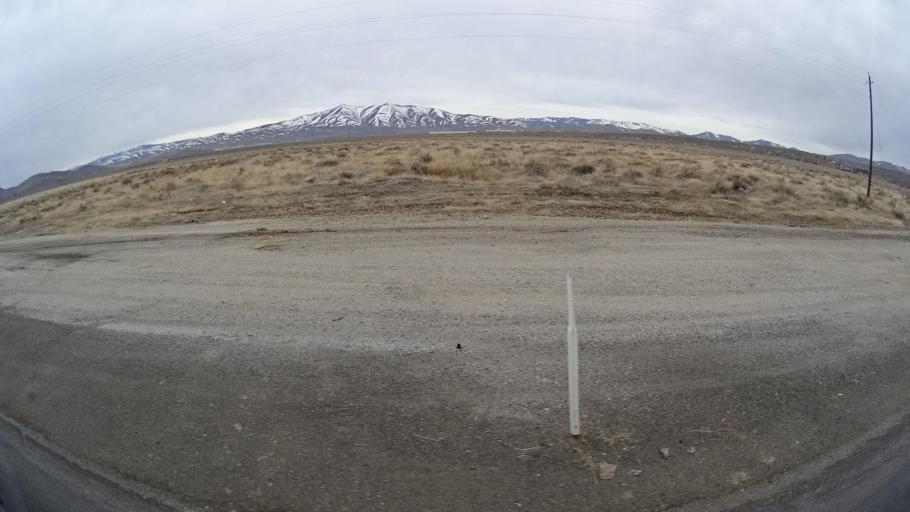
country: US
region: Nevada
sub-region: Washoe County
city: Lemmon Valley
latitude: 39.6699
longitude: -119.8325
